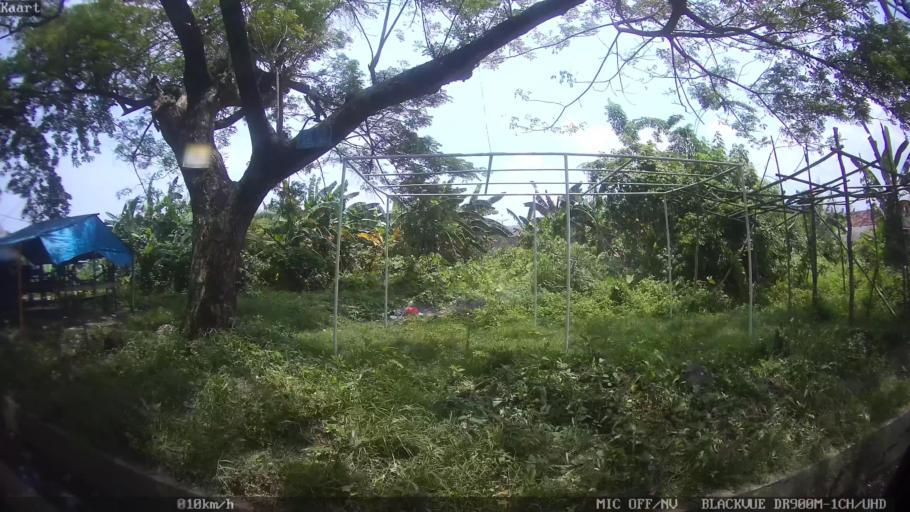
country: ID
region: Lampung
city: Bandarlampung
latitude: -5.4576
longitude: 105.2566
